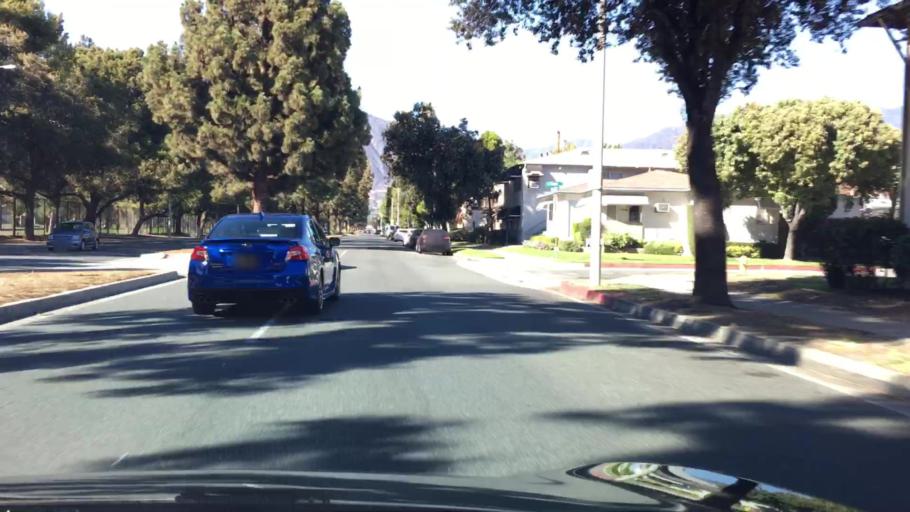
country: US
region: California
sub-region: Los Angeles County
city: Arcadia
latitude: 34.1333
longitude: -118.0313
